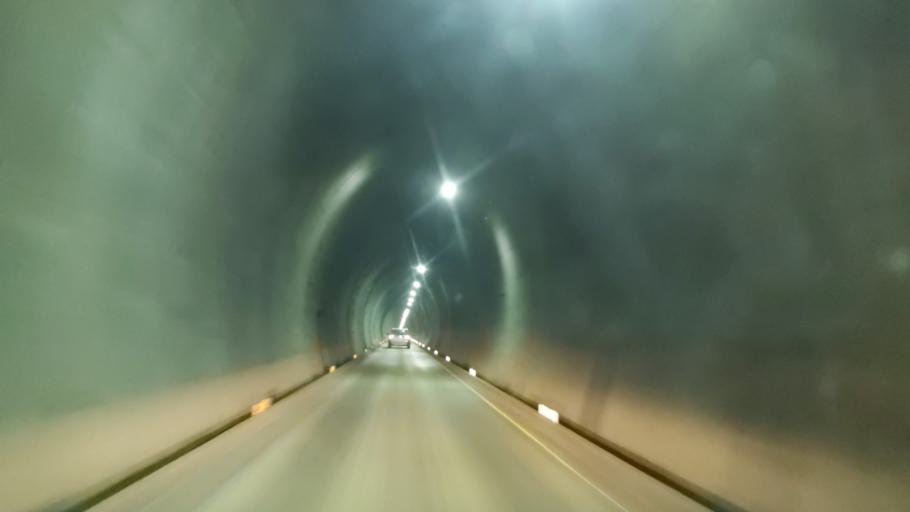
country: CL
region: Araucania
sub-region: Provincia de Cautin
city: Vilcun
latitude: -38.5300
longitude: -71.5110
